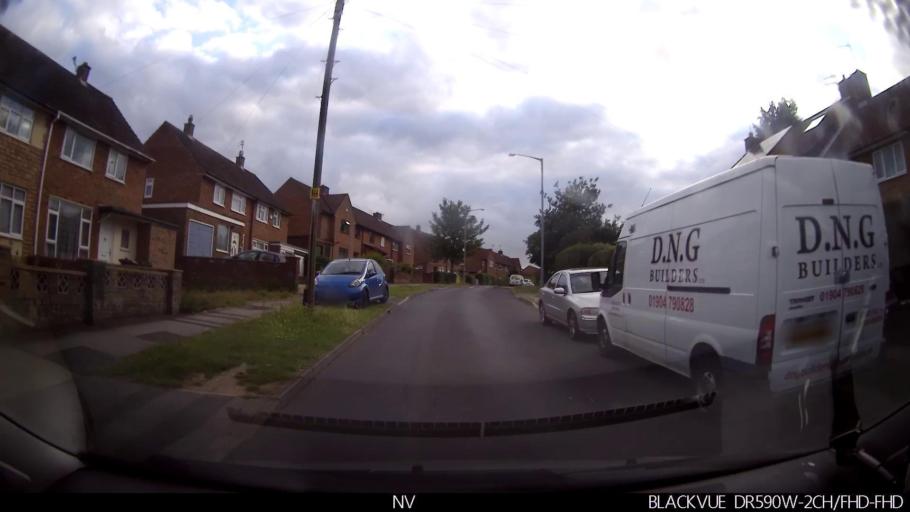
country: GB
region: England
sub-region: City of York
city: Nether Poppleton
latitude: 53.9536
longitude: -1.1380
